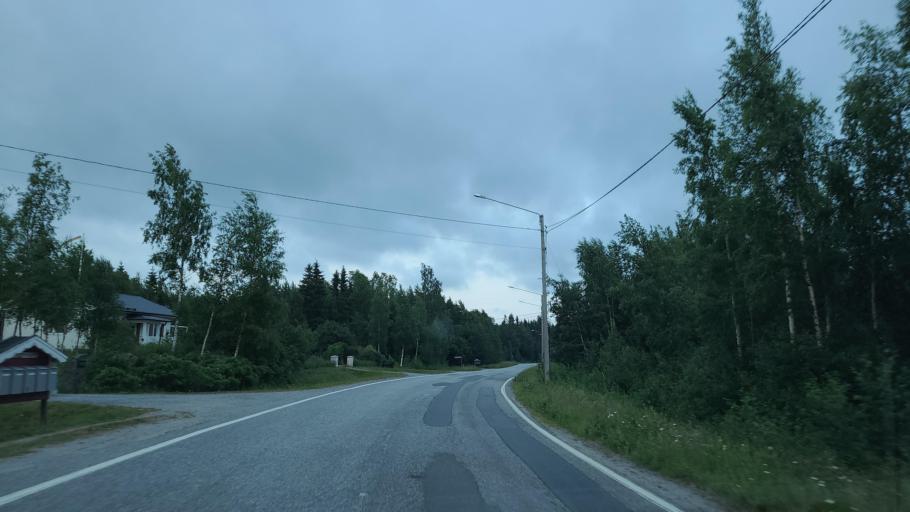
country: FI
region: Ostrobothnia
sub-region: Vaasa
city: Replot
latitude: 63.2811
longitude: 21.1293
